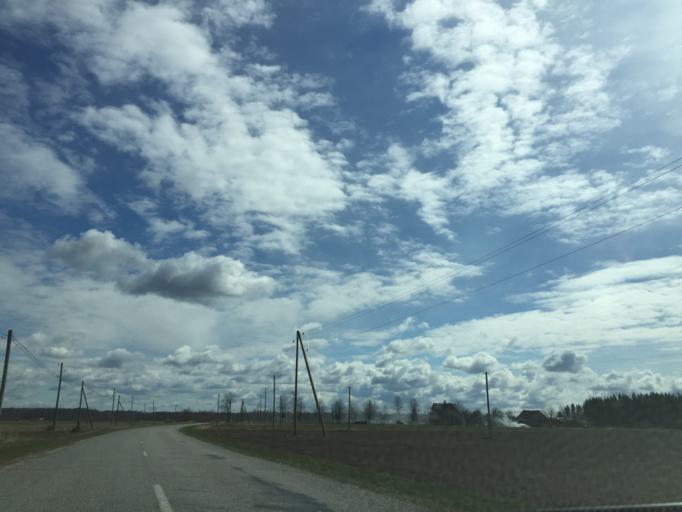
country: LV
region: Salacgrivas
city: Salacgriva
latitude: 57.7458
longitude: 24.3875
